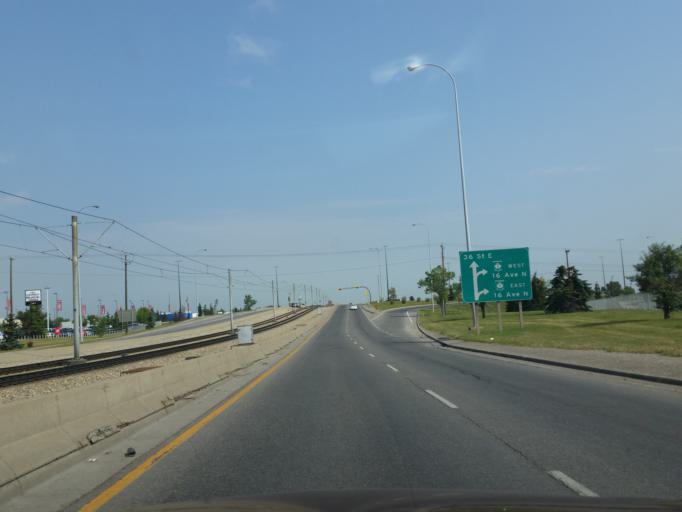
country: CA
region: Alberta
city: Calgary
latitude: 51.0634
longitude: -113.9815
